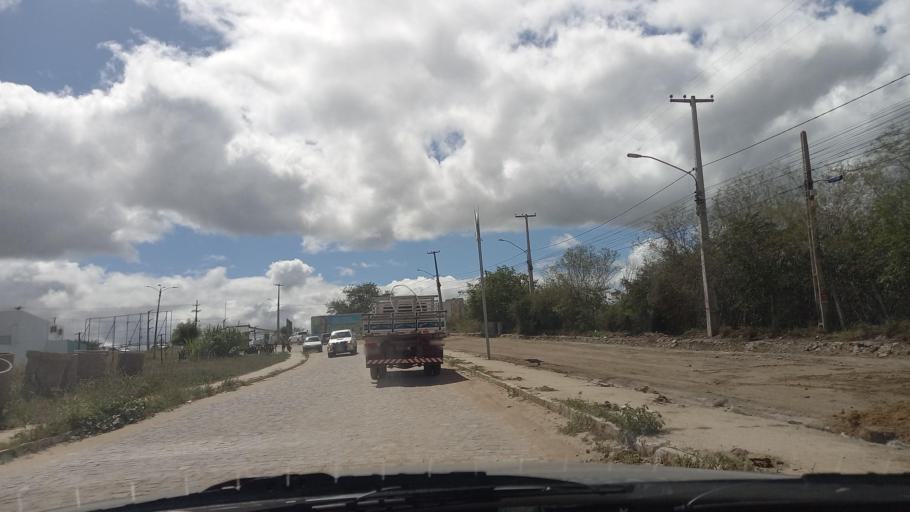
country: BR
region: Pernambuco
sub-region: Caruaru
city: Caruaru
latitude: -8.2592
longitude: -35.9553
